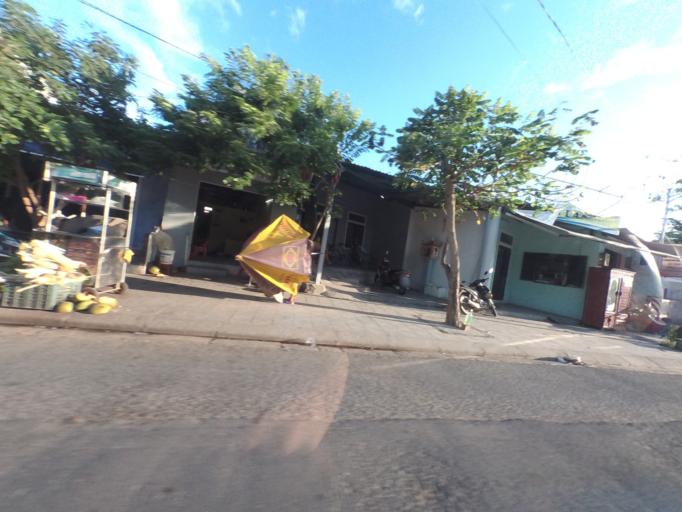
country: VN
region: Thua Thien-Hue
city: Hue
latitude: 16.4886
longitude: 107.5870
